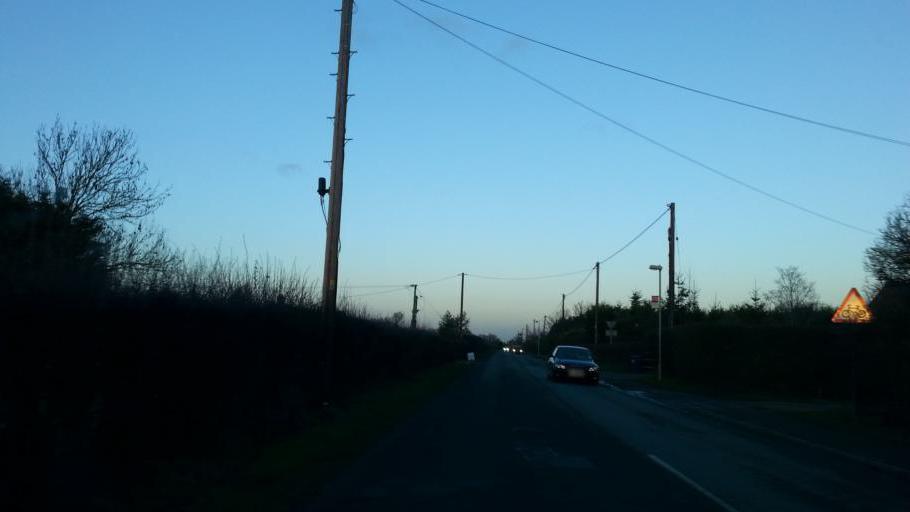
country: GB
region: England
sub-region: Cambridgeshire
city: Needingworth
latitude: 52.2931
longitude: -0.0564
